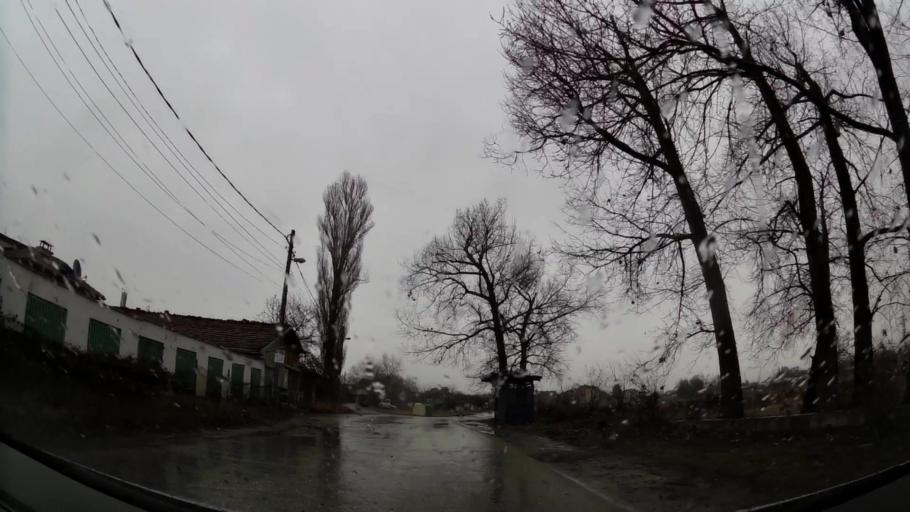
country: BG
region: Sofia-Capital
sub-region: Stolichna Obshtina
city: Sofia
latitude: 42.6599
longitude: 23.4232
